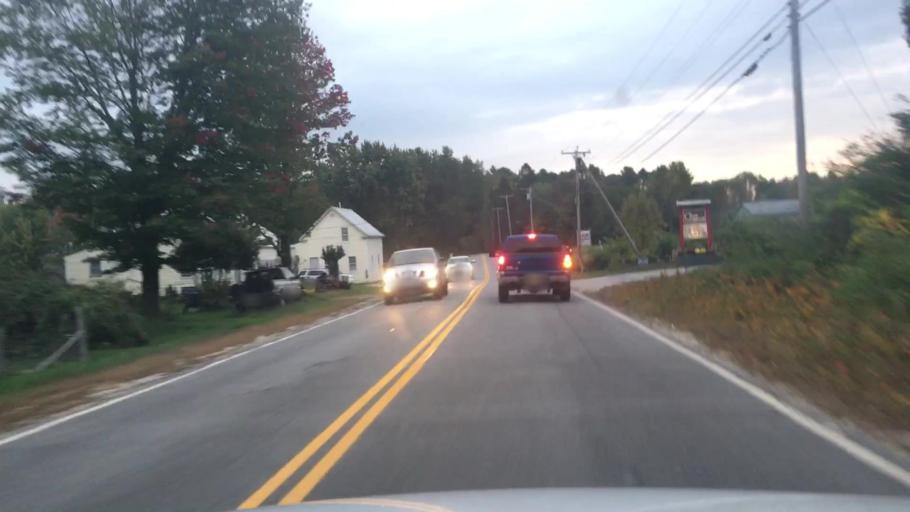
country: US
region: Maine
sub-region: York County
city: Buxton
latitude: 43.6348
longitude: -70.5134
